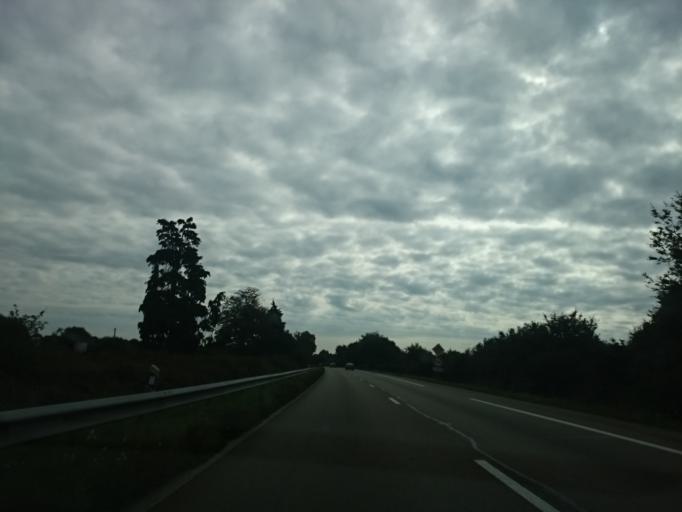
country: FR
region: Pays de la Loire
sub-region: Departement de la Loire-Atlantique
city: Malville
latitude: 47.3461
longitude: -1.8630
